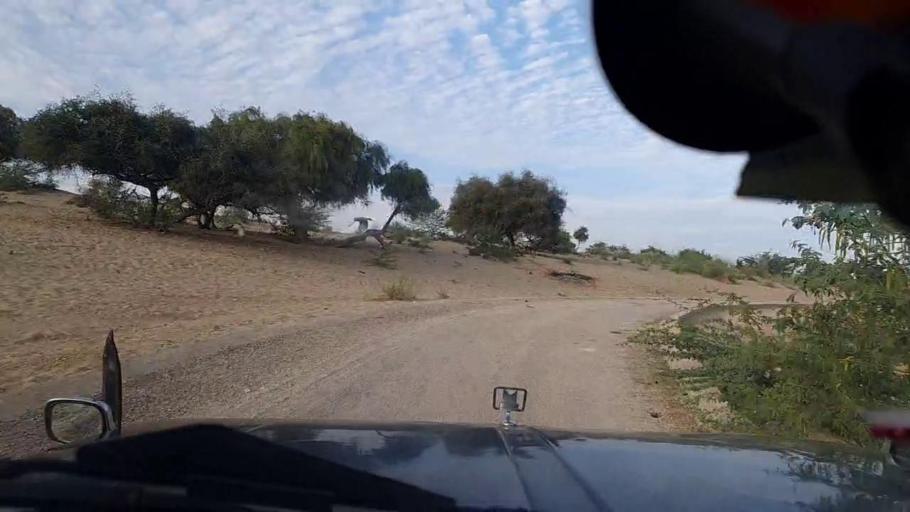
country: PK
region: Sindh
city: Diplo
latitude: 24.4692
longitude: 69.7901
